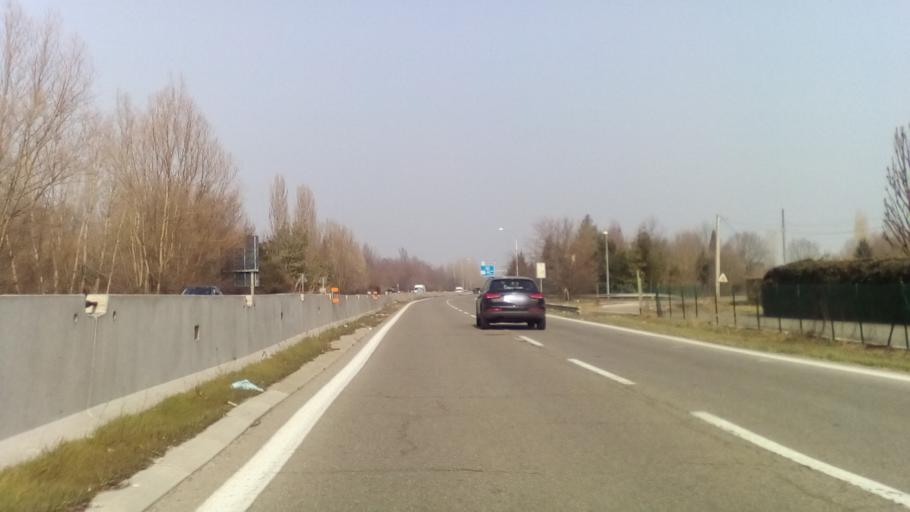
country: IT
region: Emilia-Romagna
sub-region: Provincia di Modena
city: Modena
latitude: 44.6219
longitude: 10.9459
